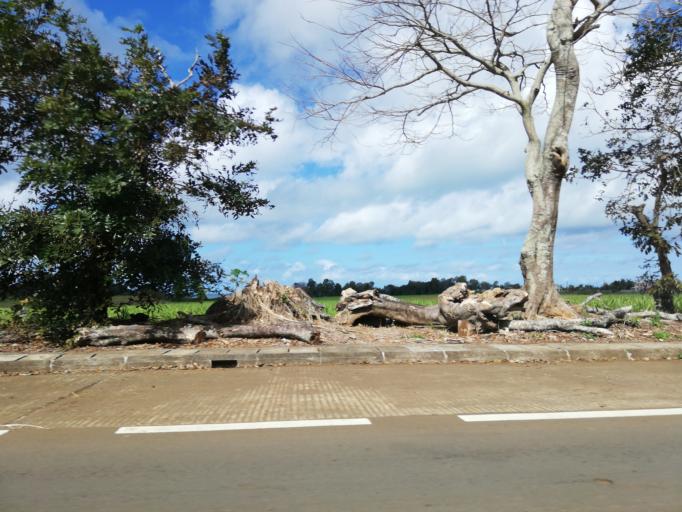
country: MU
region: Grand Port
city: Mahebourg
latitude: -20.3851
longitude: 57.6968
